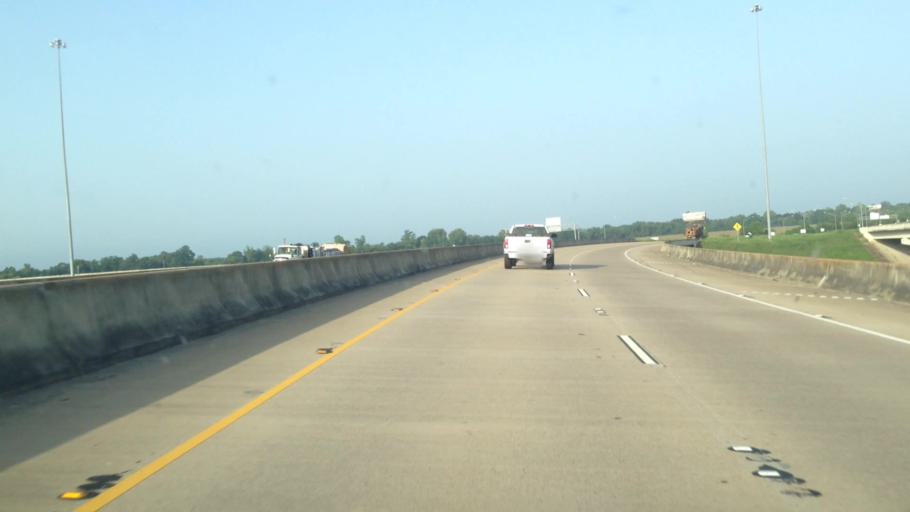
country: US
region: Louisiana
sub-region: Rapides Parish
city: Alexandria
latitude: 31.2421
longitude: -92.4313
